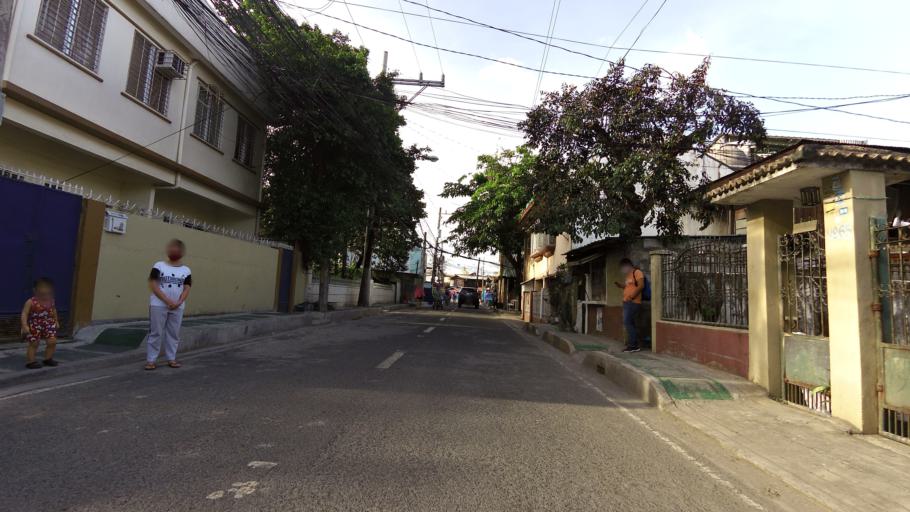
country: PH
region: Calabarzon
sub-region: Province of Rizal
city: Pateros
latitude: 14.5651
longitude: 121.0838
